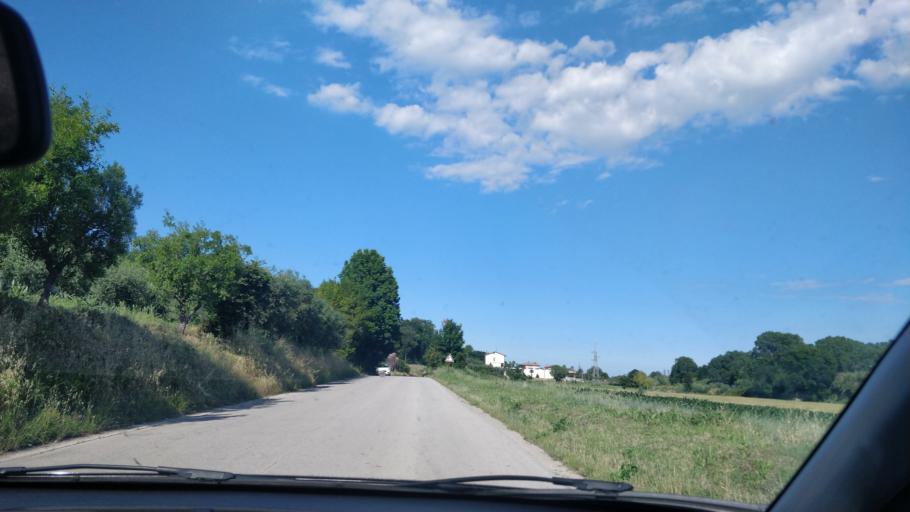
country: IT
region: The Marches
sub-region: Provincia di Ascoli Piceno
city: Massignano
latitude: 43.0371
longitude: 13.8052
